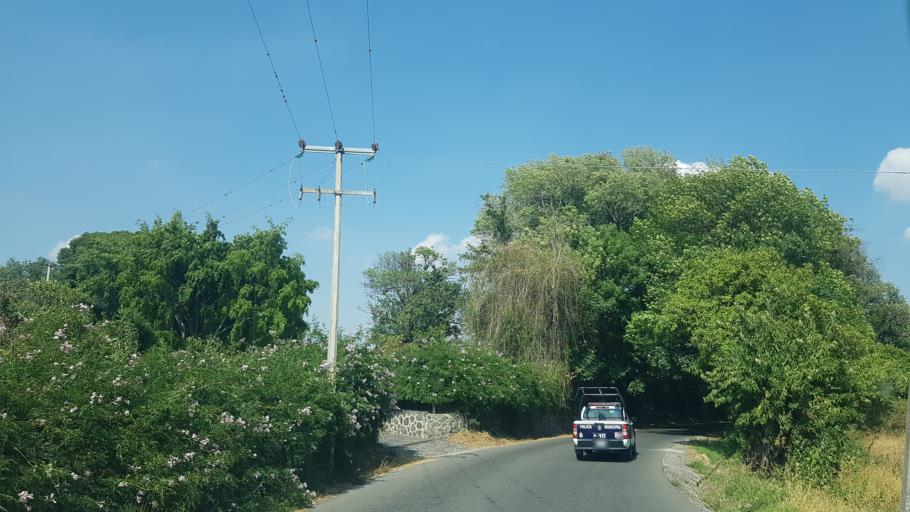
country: MX
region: Puebla
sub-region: Atlixco
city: Colonia Agricola de Ocotepec (Colonia San Jose)
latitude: 18.9216
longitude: -98.5402
